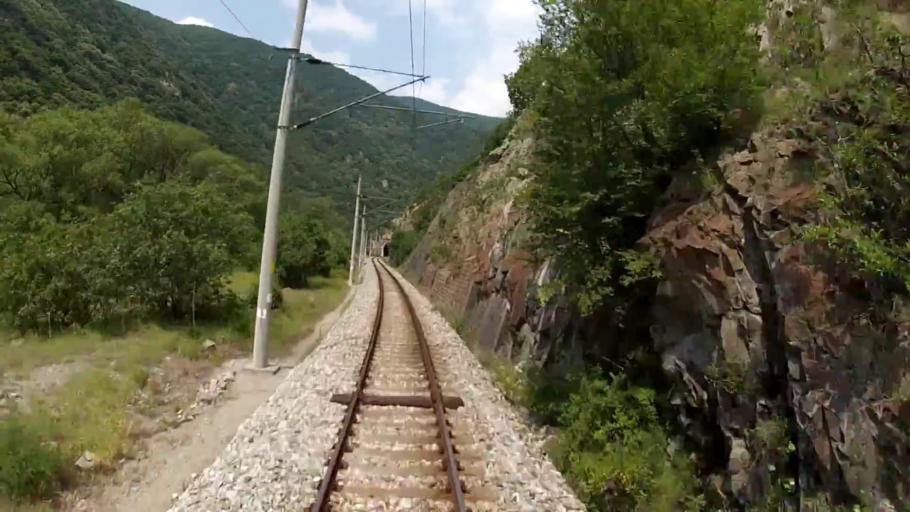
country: BG
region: Blagoevgrad
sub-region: Obshtina Kresna
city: Stara Kresna
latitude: 41.8138
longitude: 23.1608
